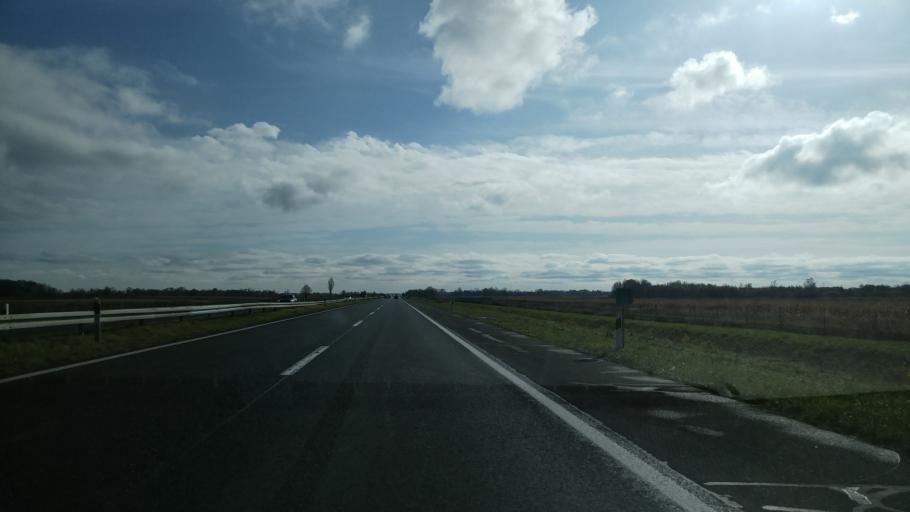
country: HR
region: Zagrebacka
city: Lupoglav
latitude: 45.7282
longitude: 16.3396
